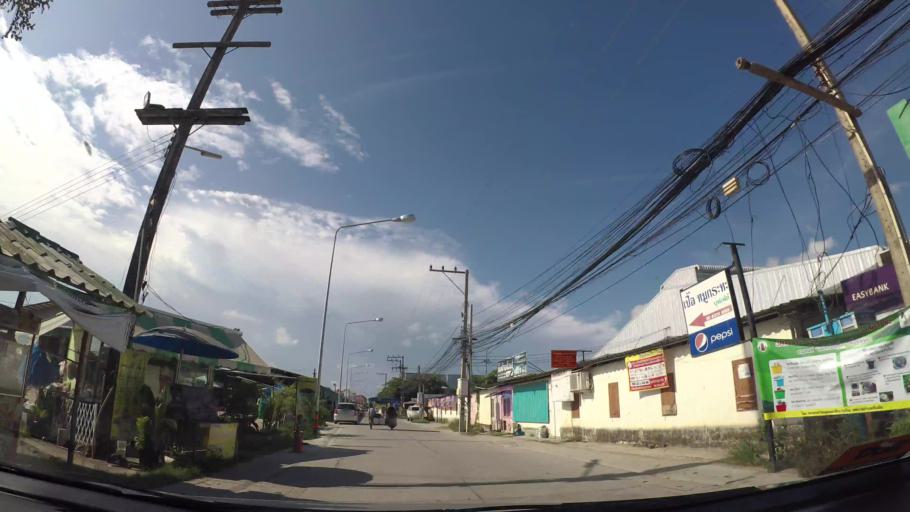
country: TH
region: Rayong
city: Rayong
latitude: 12.6659
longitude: 101.2983
